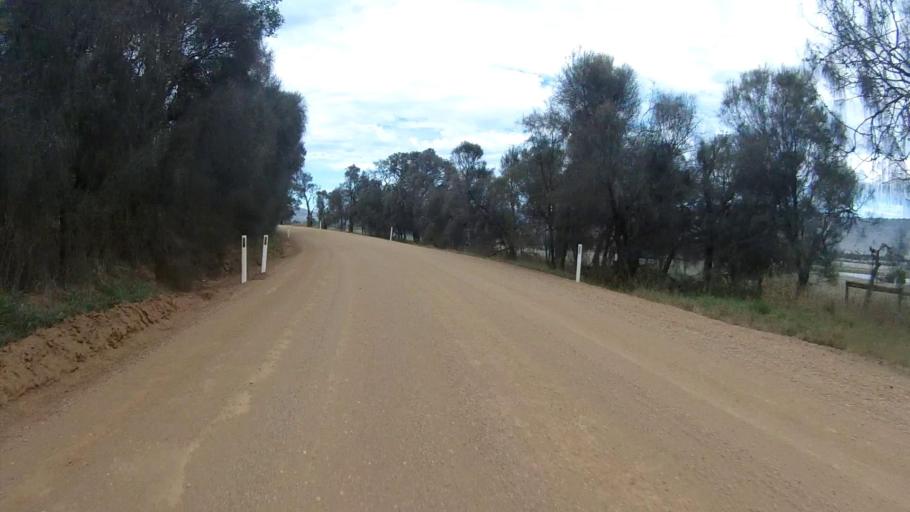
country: AU
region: Tasmania
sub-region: Sorell
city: Sorell
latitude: -42.7003
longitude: 147.4586
